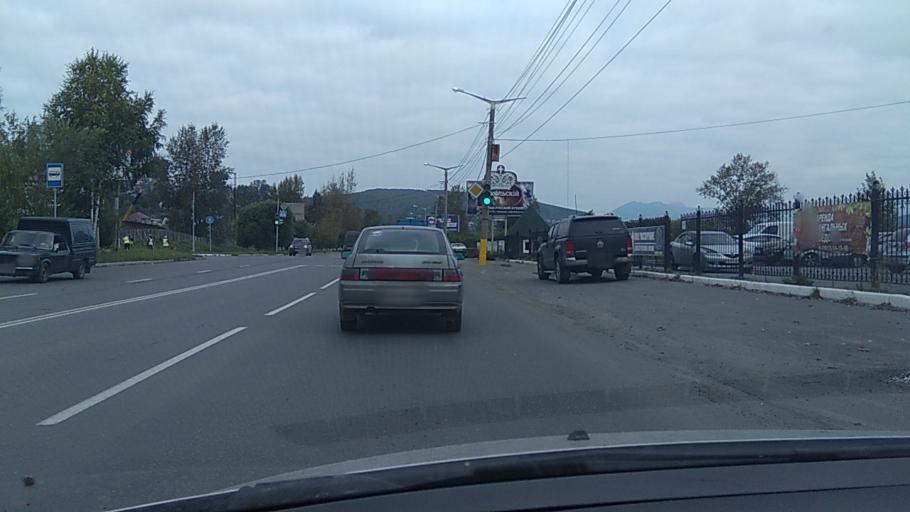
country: RU
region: Chelyabinsk
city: Zlatoust
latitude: 55.1537
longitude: 59.6791
